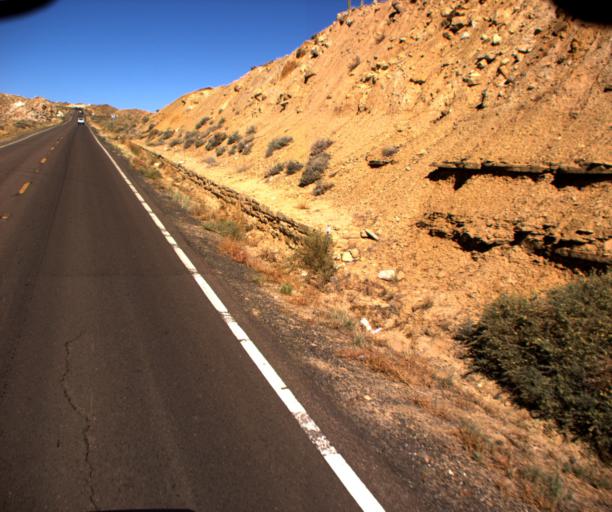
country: US
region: Arizona
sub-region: Navajo County
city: First Mesa
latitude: 35.7993
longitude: -110.5137
